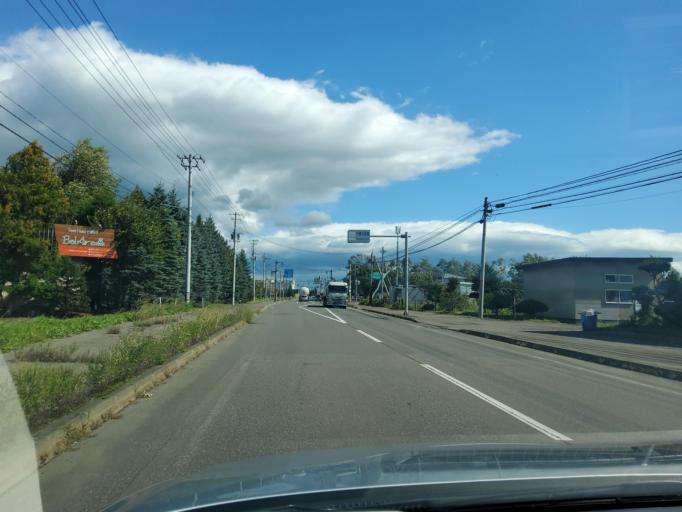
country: JP
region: Hokkaido
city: Obihiro
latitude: 42.9354
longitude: 143.2936
